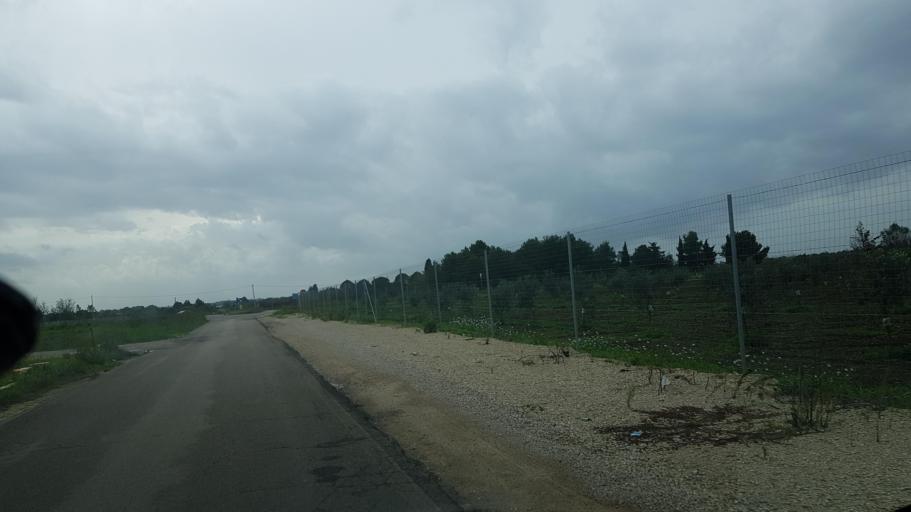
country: IT
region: Apulia
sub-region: Provincia di Lecce
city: Campi Salentina
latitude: 40.3850
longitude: 18.0224
